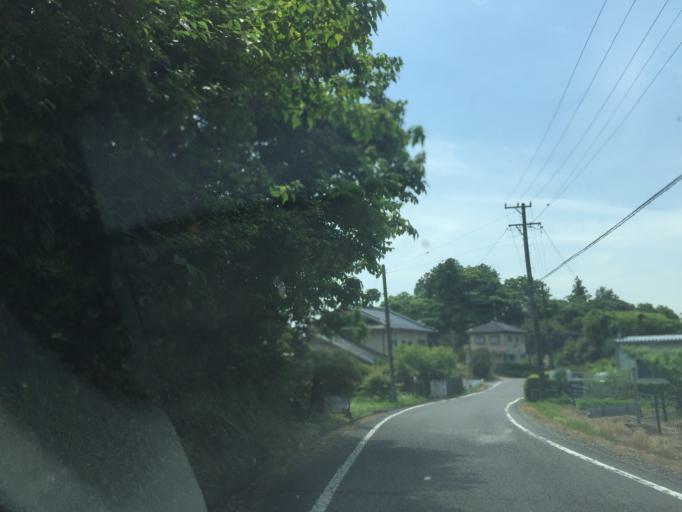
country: JP
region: Shizuoka
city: Mori
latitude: 34.7941
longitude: 137.9657
